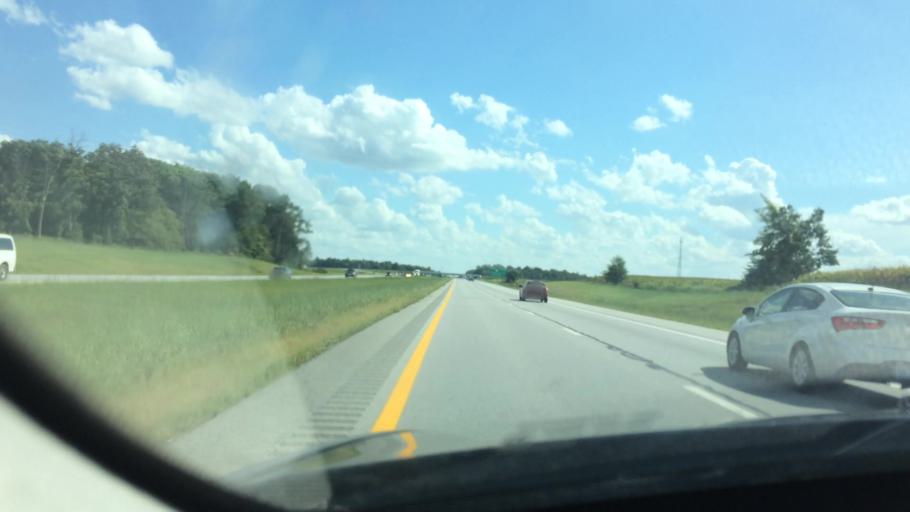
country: US
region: Ohio
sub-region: Shelby County
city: Botkins
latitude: 40.4469
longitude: -84.1695
